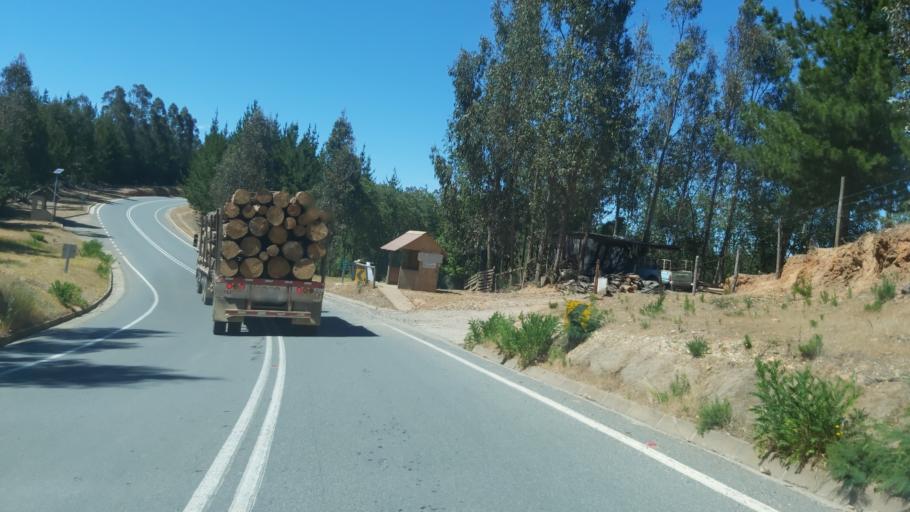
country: CL
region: Maule
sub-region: Provincia de Talca
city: Constitucion
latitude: -34.9305
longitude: -71.9872
